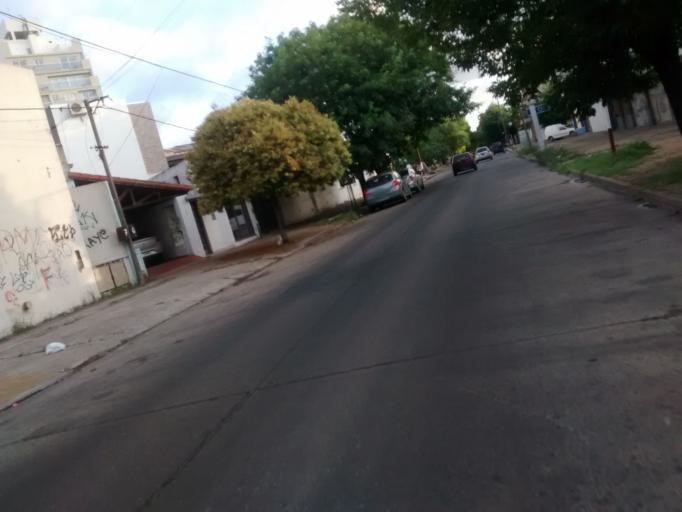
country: AR
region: Buenos Aires
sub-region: Partido de La Plata
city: La Plata
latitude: -34.9146
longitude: -57.9671
